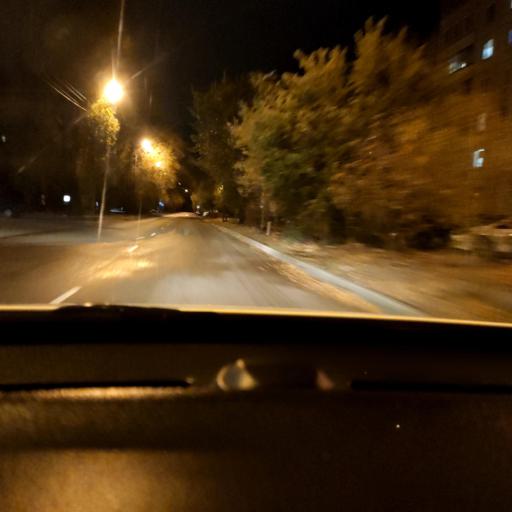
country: RU
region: Voronezj
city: Maslovka
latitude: 51.6331
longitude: 39.2829
